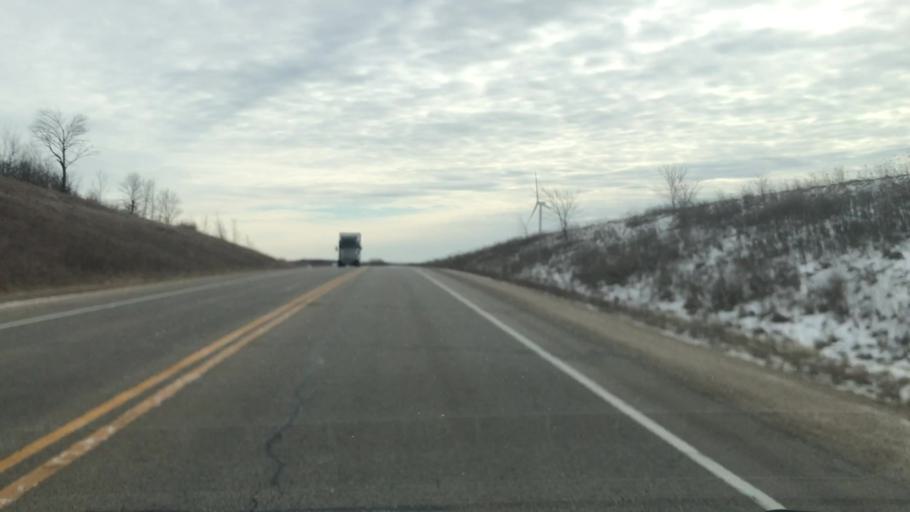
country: US
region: Wisconsin
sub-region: Dodge County
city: Theresa
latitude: 43.4376
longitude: -88.4764
